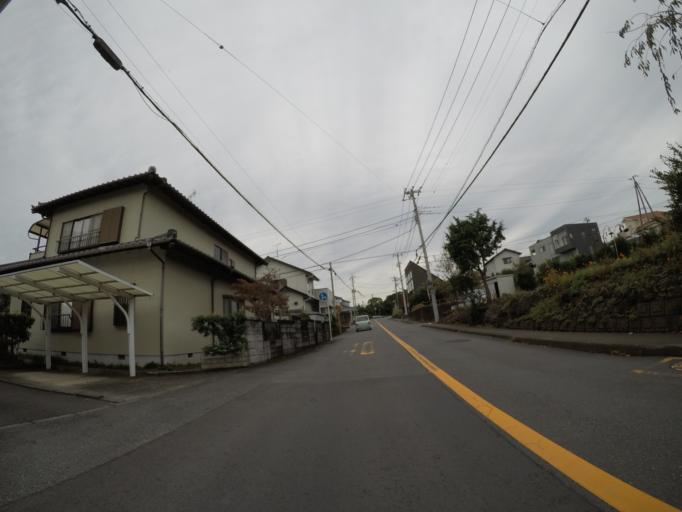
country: JP
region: Shizuoka
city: Fuji
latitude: 35.1885
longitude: 138.6945
